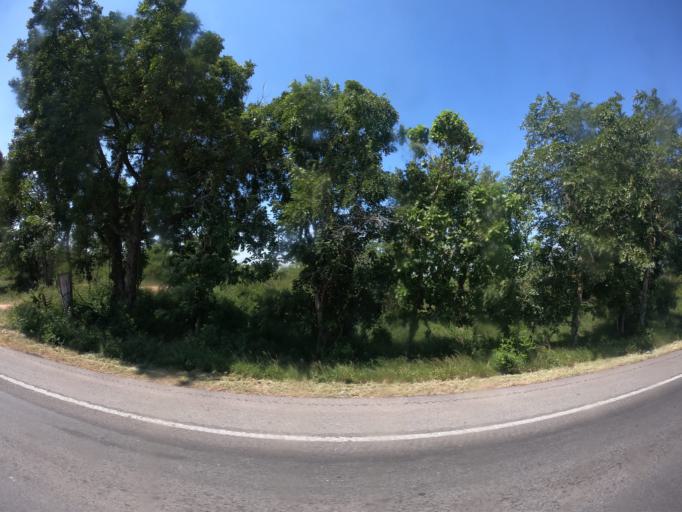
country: TH
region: Khon Kaen
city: Non Sila
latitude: 15.9078
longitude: 102.6561
